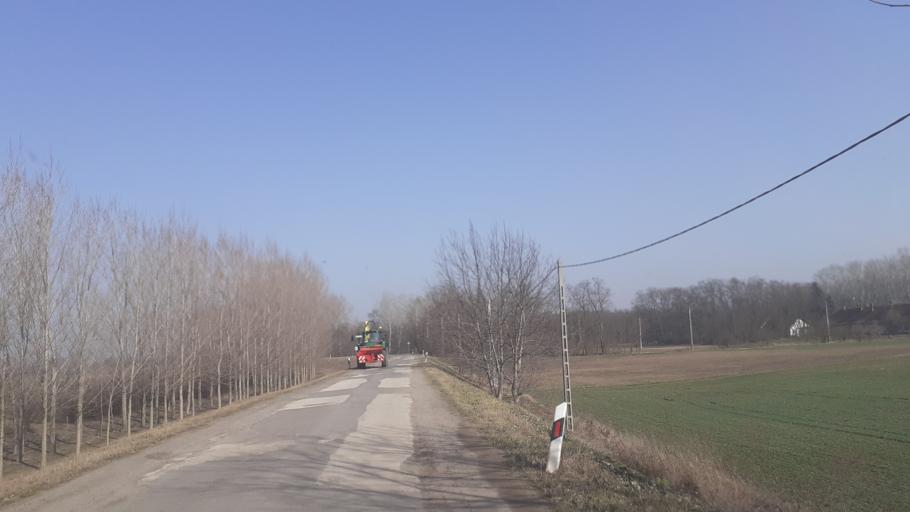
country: HU
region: Pest
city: Domsod
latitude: 47.0708
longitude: 19.0002
